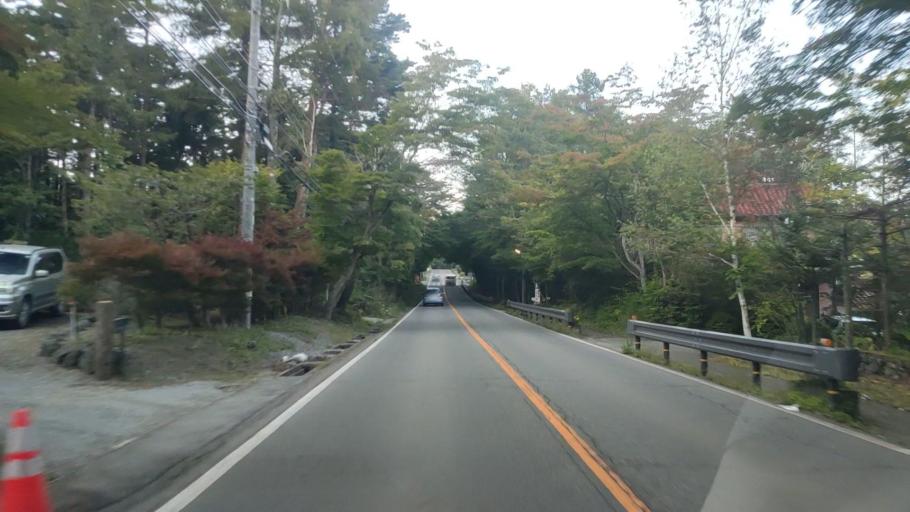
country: JP
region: Nagano
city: Komoro
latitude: 36.3709
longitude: 138.5876
